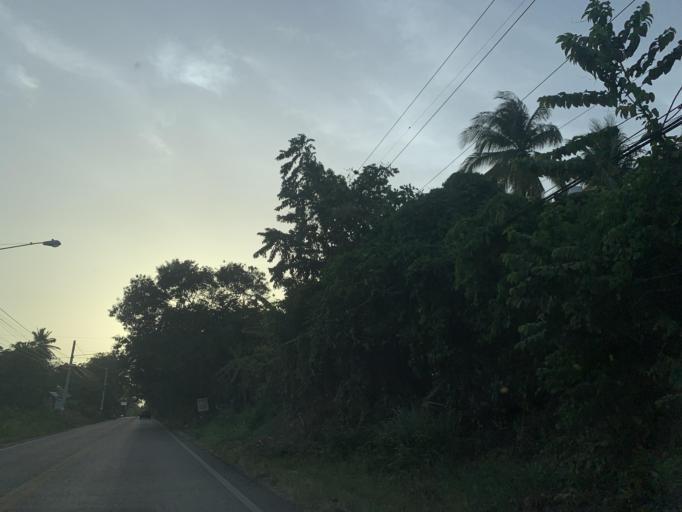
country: DO
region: Puerto Plata
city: Cabarete
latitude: 19.7743
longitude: -70.4450
